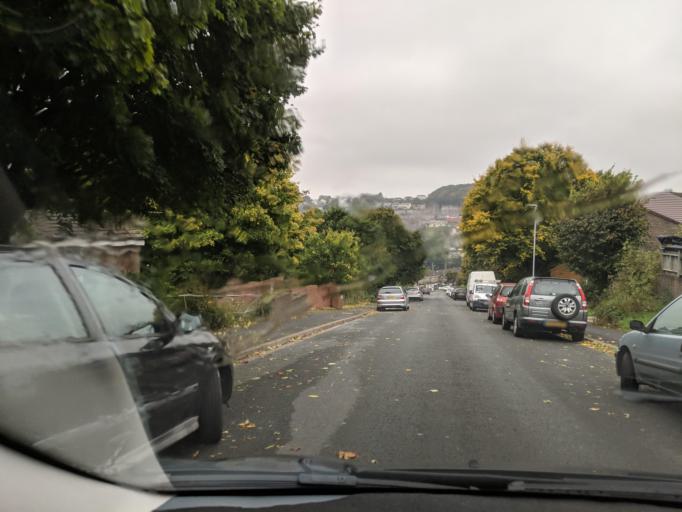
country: GB
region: England
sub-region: Devon
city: Plympton
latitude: 50.4079
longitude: -4.0993
